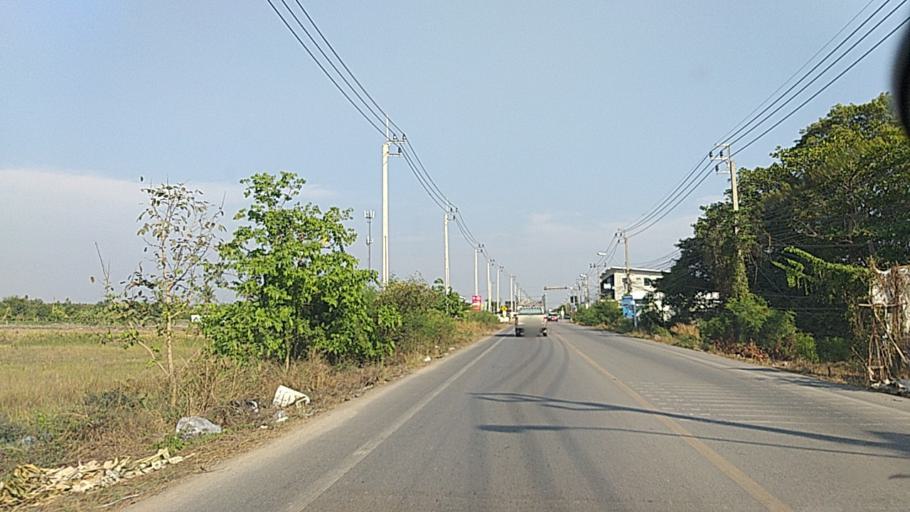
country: TH
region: Nonthaburi
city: Sai Noi
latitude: 13.9460
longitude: 100.3545
